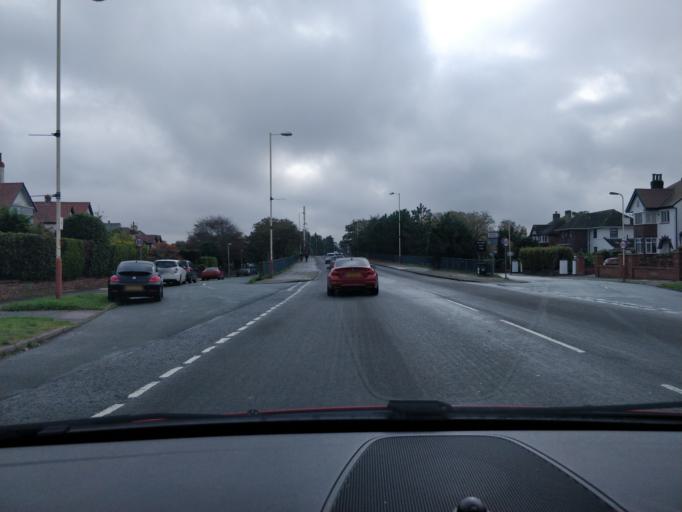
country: GB
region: England
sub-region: Sefton
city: Southport
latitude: 53.6237
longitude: -3.0267
